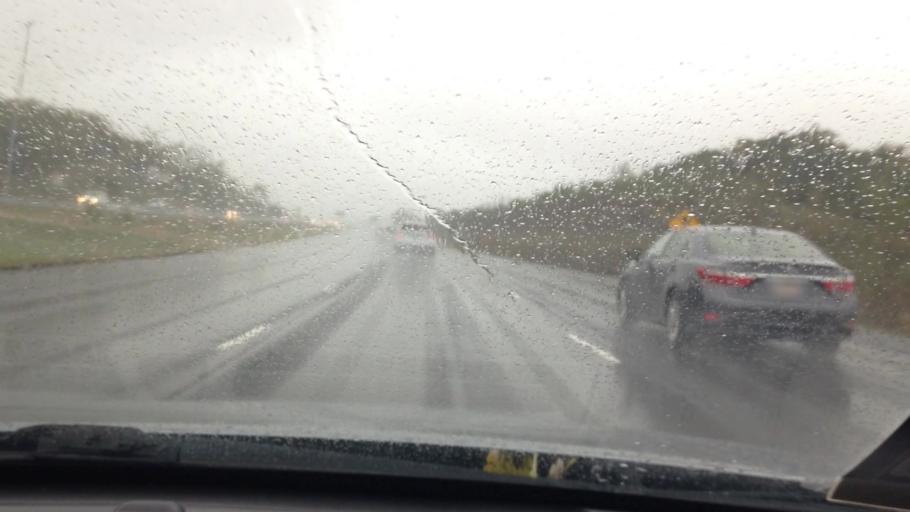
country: US
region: Kansas
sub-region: Wyandotte County
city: Edwardsville
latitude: 39.1563
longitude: -94.8213
